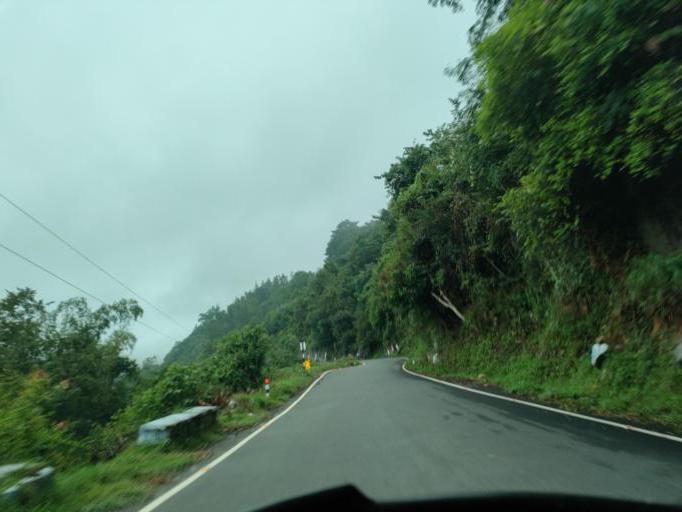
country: IN
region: Tamil Nadu
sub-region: Dindigul
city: Ayakudi
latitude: 10.3600
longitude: 77.5530
